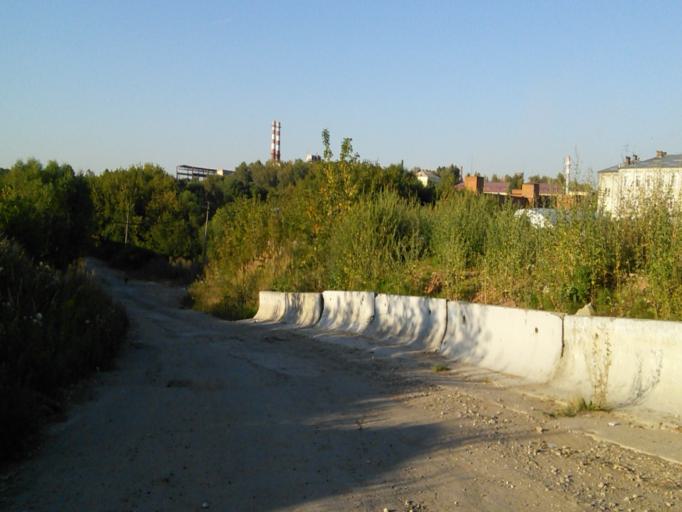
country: RU
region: Moskovskaya
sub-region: Podol'skiy Rayon
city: Podol'sk
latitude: 55.4526
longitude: 37.5615
